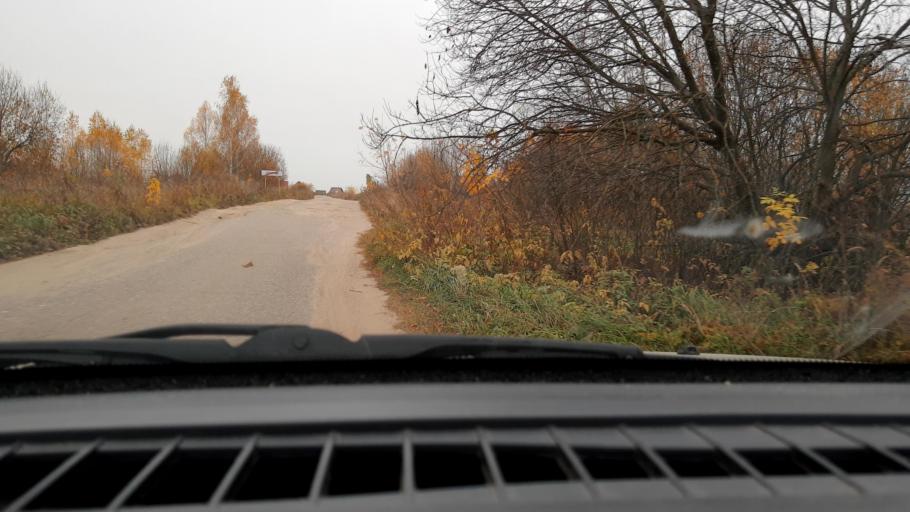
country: RU
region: Nizjnij Novgorod
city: Burevestnik
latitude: 56.0475
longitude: 43.8439
